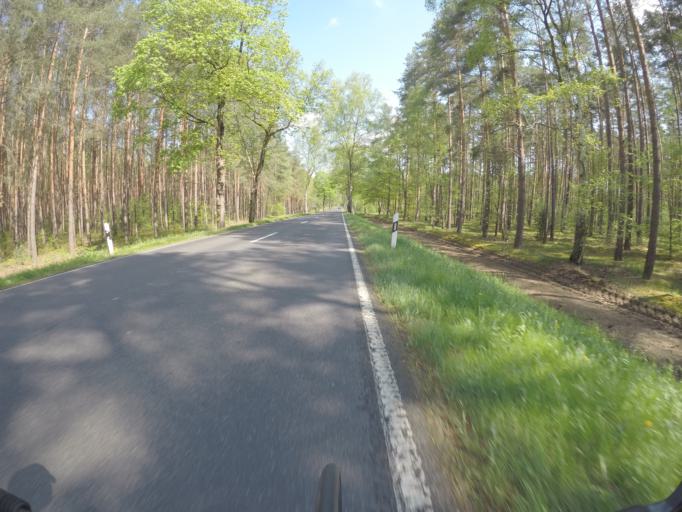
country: DE
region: Brandenburg
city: Marienwerder
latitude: 52.8050
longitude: 13.5530
